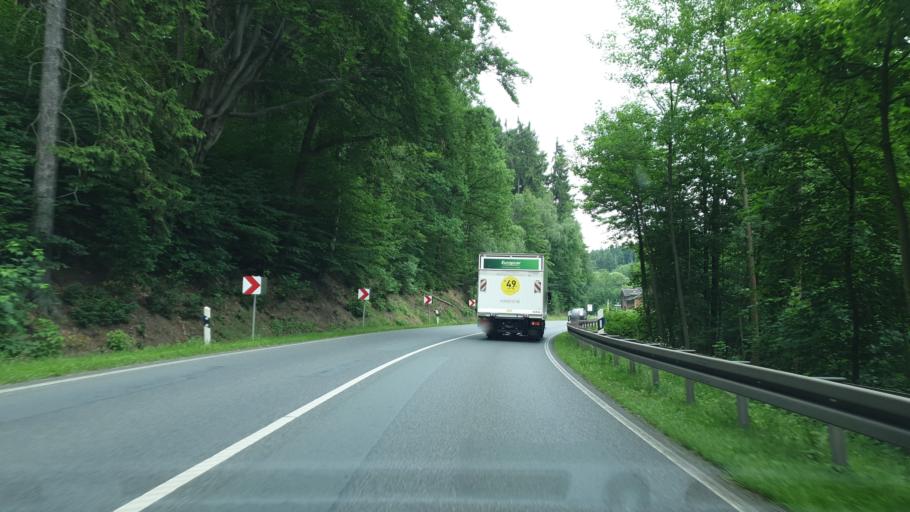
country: DE
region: Saxony
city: Lengenfeld
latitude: 50.5554
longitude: 12.3840
